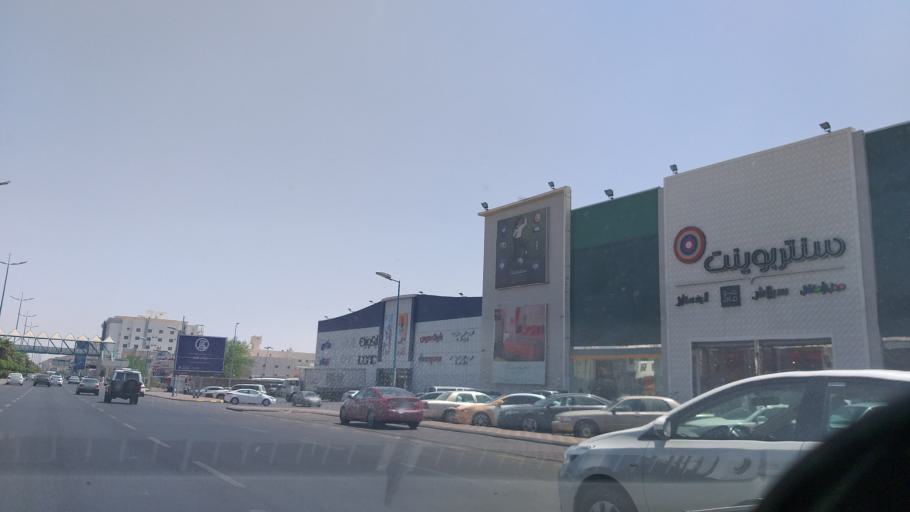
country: SA
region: Makkah
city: Ta'if
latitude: 21.2910
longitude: 40.4238
